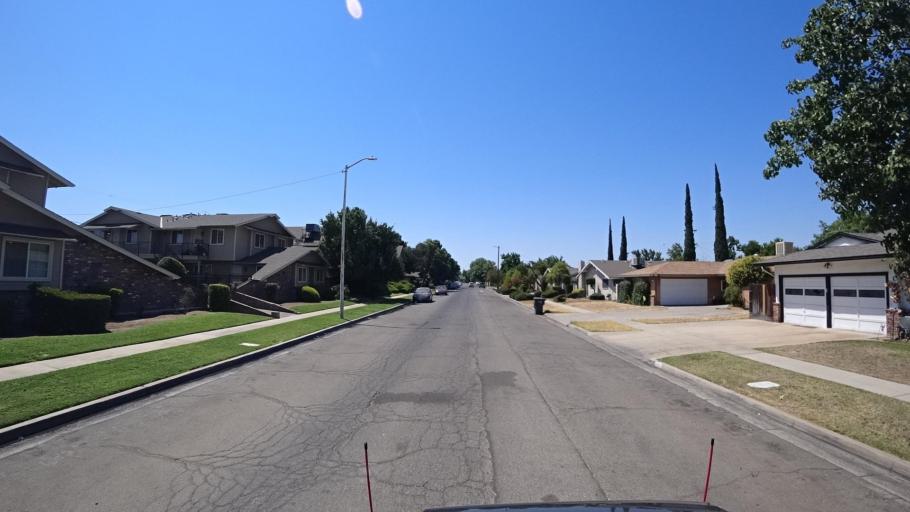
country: US
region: California
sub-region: Fresno County
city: Fresno
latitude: 36.8002
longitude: -119.7566
